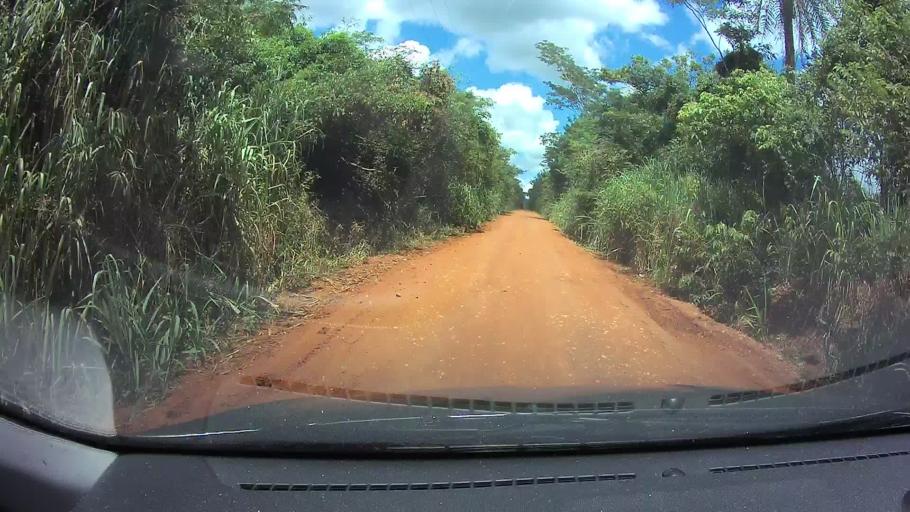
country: PY
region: Paraguari
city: La Colmena
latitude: -25.9036
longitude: -56.7935
